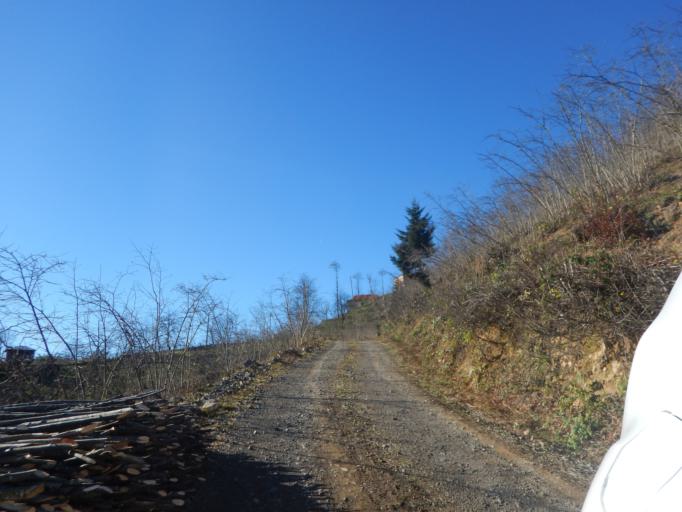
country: TR
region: Ordu
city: Kabaduz
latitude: 40.8438
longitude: 37.9177
